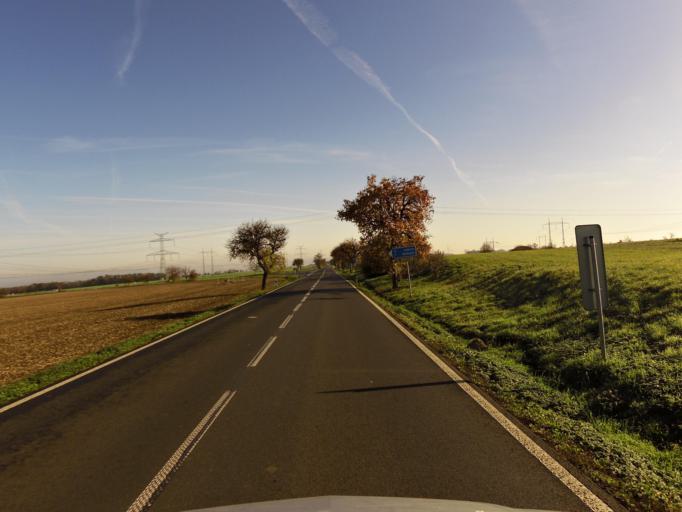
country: CZ
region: Ustecky
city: Brezno
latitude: 50.3339
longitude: 13.3720
